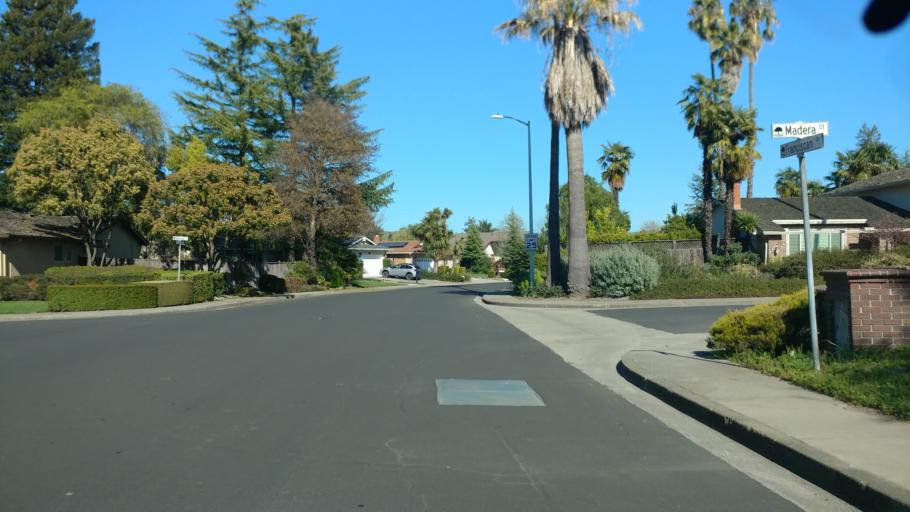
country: US
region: California
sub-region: Contra Costa County
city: San Ramon
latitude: 37.7854
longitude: -121.9764
